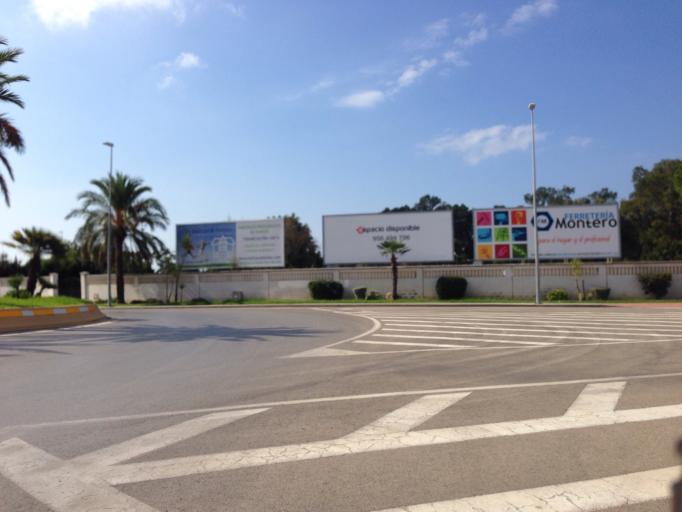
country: ES
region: Andalusia
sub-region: Provincia de Cadiz
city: Chiclana de la Frontera
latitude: 36.4075
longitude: -6.1662
